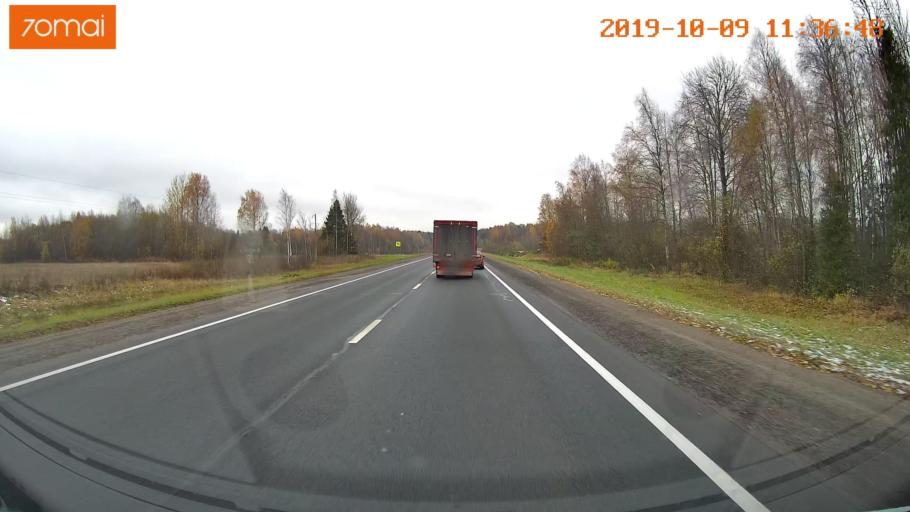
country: RU
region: Vologda
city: Gryazovets
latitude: 58.9858
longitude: 40.1411
